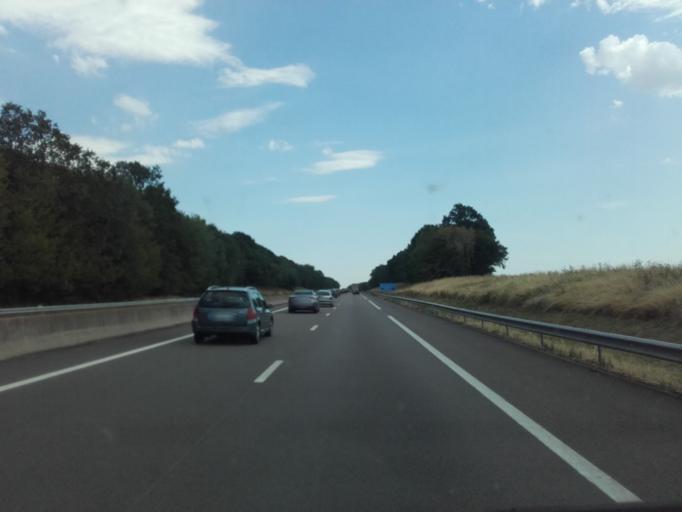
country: FR
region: Bourgogne
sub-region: Departement de la Cote-d'Or
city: Semur-en-Auxois
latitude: 47.4615
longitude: 4.2526
